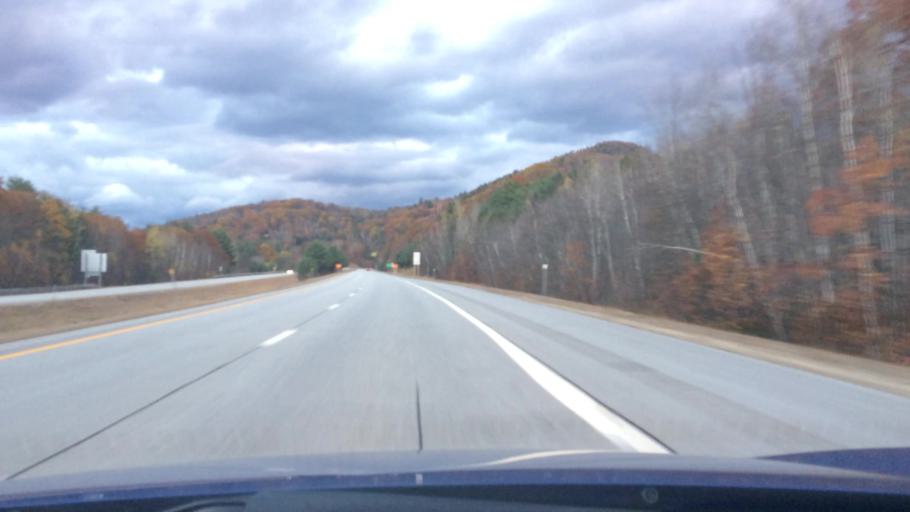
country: US
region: New Hampshire
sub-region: Grafton County
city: Woodstock
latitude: 43.9633
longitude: -71.6773
